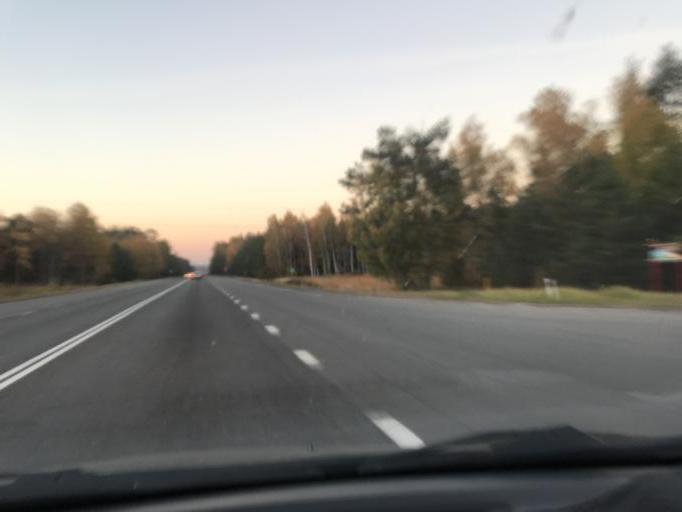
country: BY
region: Mogilev
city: Babruysk
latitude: 53.1648
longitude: 29.0454
